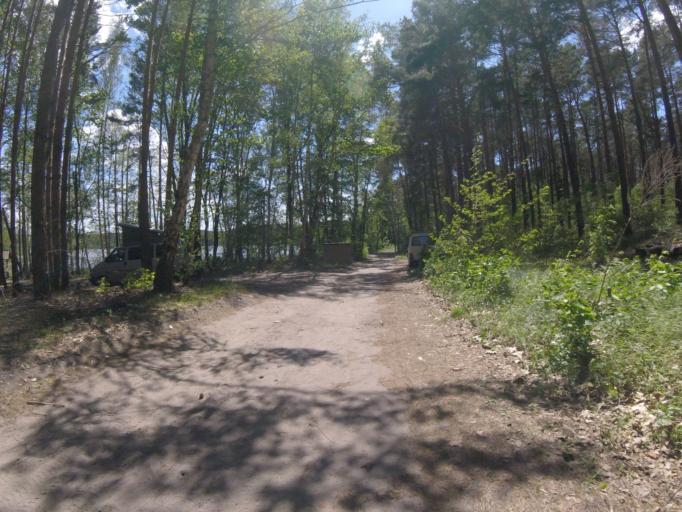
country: DE
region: Brandenburg
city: Teupitz
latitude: 52.1184
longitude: 13.6110
